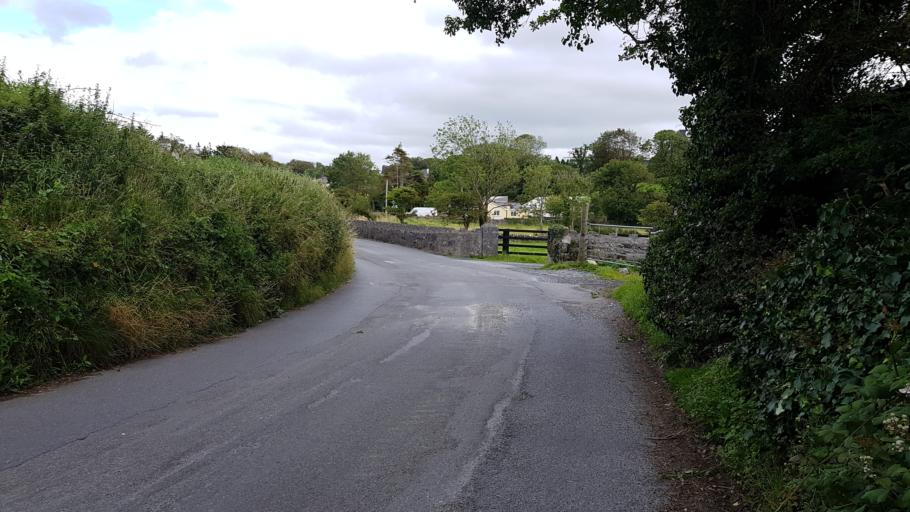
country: IE
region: Connaught
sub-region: County Galway
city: Gaillimh
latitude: 53.2964
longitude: -9.0197
